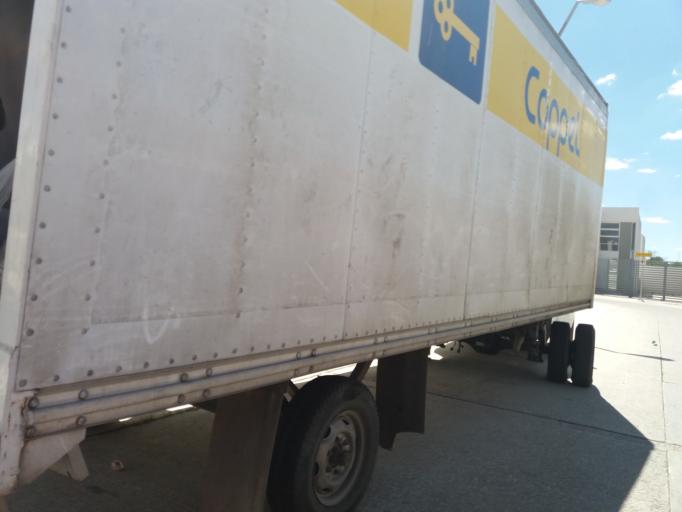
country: MX
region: Aguascalientes
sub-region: Aguascalientes
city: San Sebastian [Fraccionamiento]
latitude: 21.8306
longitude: -102.3024
